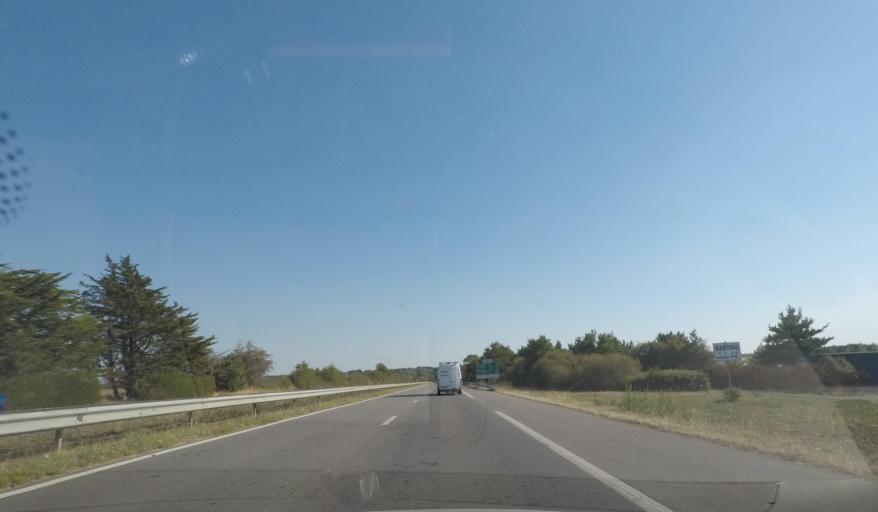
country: FR
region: Pays de la Loire
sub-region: Departement de la Loire-Atlantique
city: Saint-Michel-Chef-Chef
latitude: 47.1709
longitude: -2.1441
